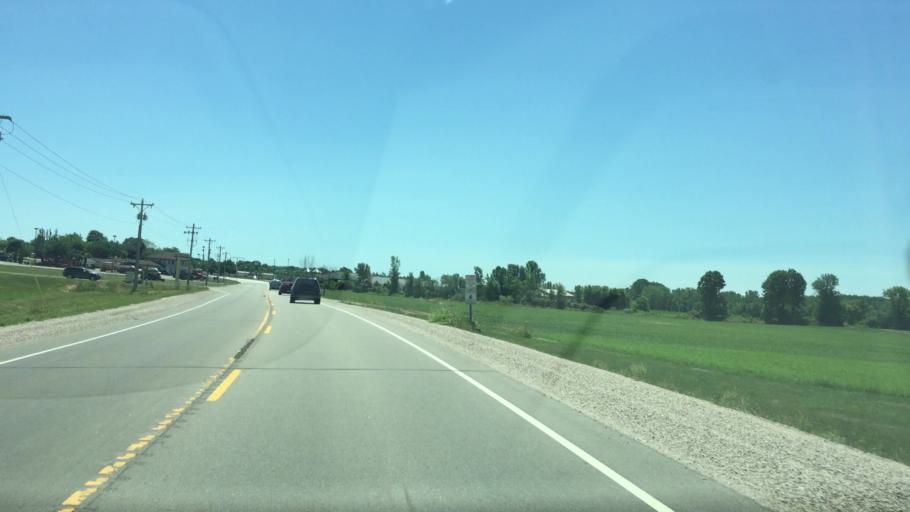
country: US
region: Wisconsin
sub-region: Calumet County
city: New Holstein
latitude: 43.9598
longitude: -88.1112
